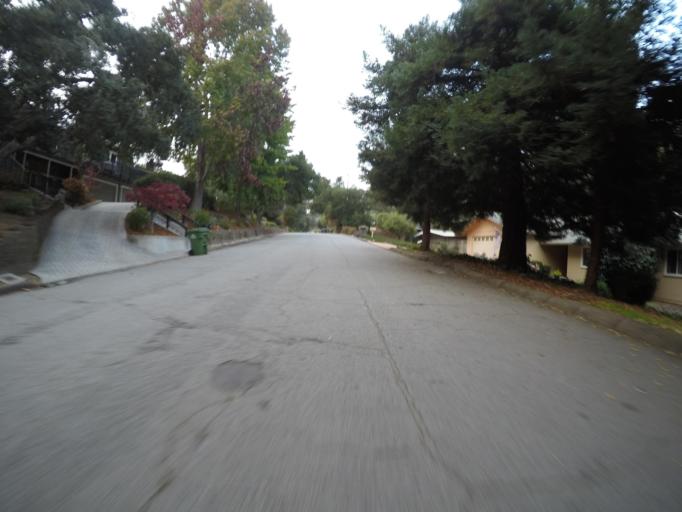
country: US
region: California
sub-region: Santa Cruz County
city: Pasatiempo
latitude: 37.0210
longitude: -122.0340
